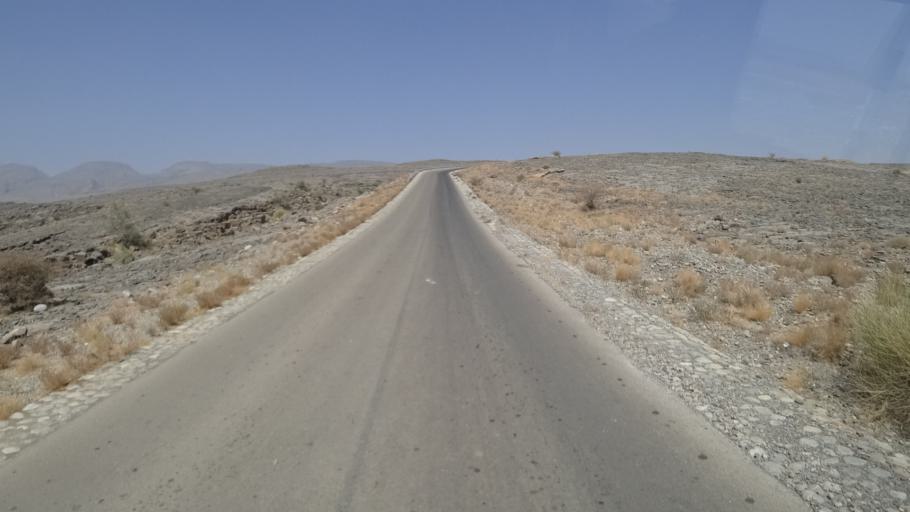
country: OM
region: Muhafazat ad Dakhiliyah
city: Bahla'
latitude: 23.1011
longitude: 57.3497
